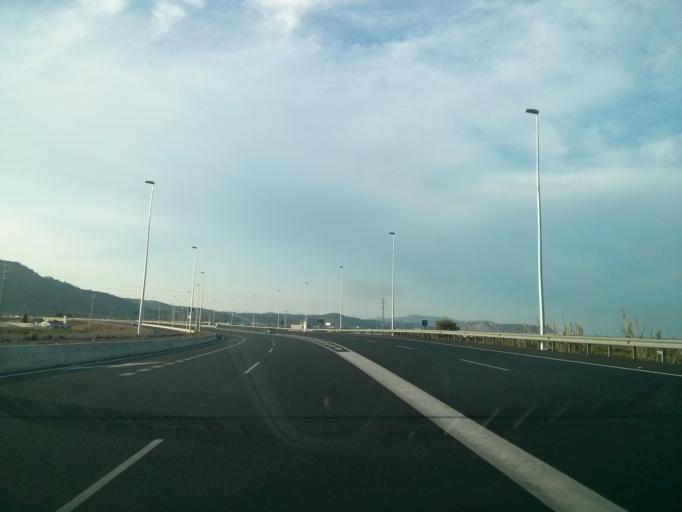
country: ES
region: Valencia
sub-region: Provincia de Valencia
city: Pucol
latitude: 39.6226
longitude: -0.2951
